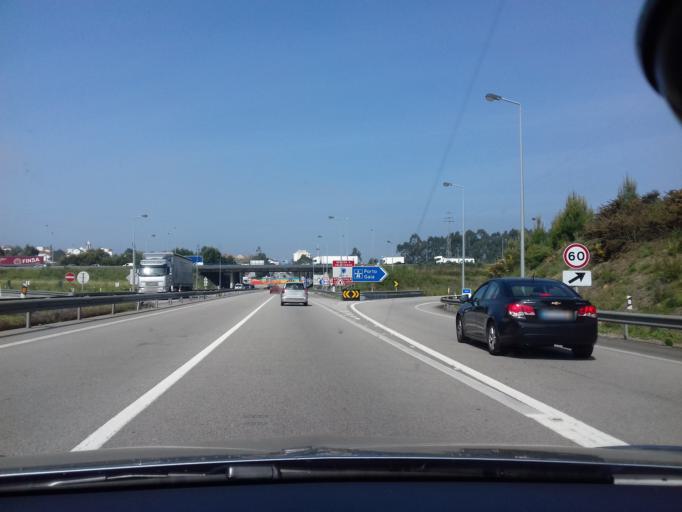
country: PT
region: Aveiro
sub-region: Espinho
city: Silvalde
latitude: 41.0086
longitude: -8.6163
